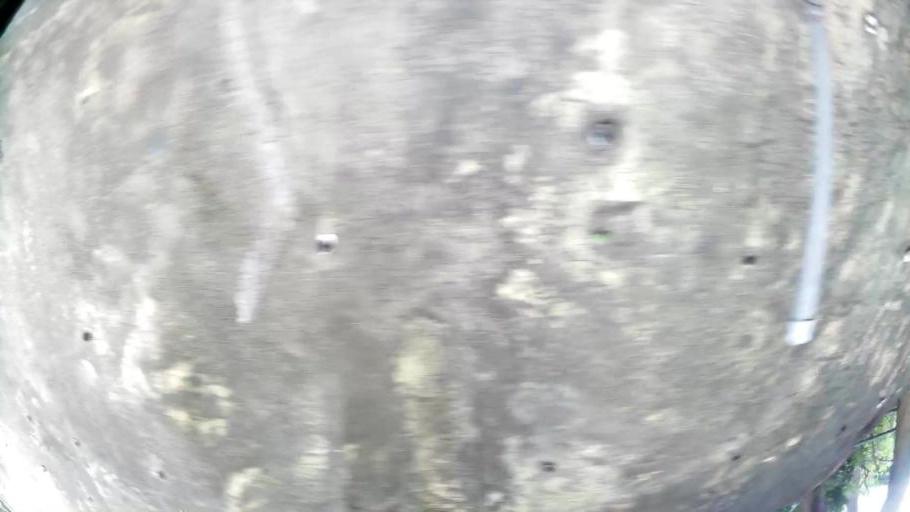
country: HK
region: Wanchai
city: Wan Chai
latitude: 22.2682
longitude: 114.1900
